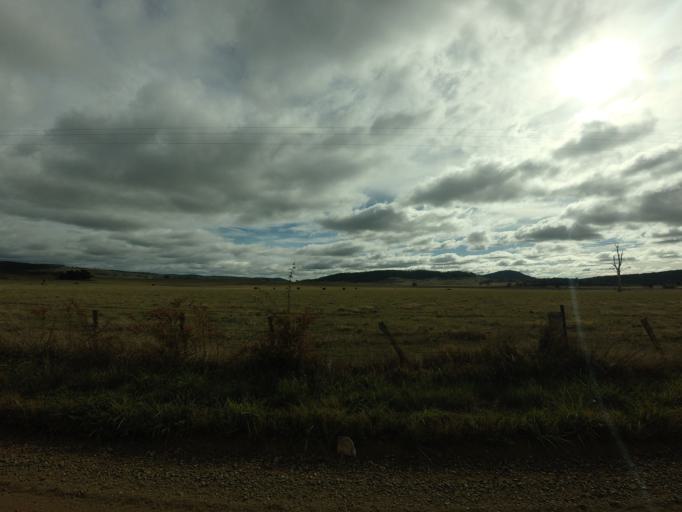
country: AU
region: Tasmania
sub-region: Brighton
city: Bridgewater
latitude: -42.4203
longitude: 147.3925
